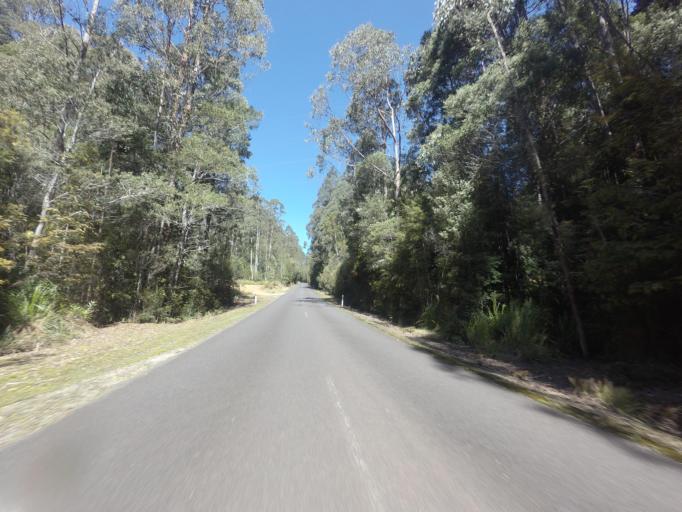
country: AU
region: Tasmania
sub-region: Huon Valley
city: Geeveston
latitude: -42.8231
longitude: 146.3136
